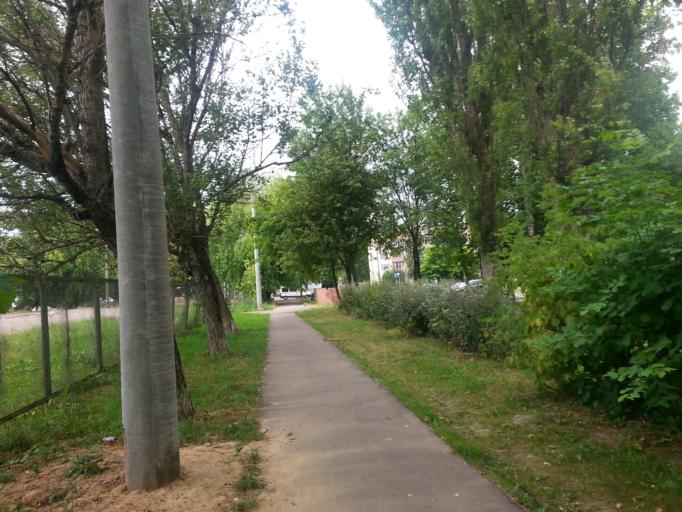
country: BY
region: Minsk
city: Novoye Medvezhino
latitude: 53.9144
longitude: 27.4914
